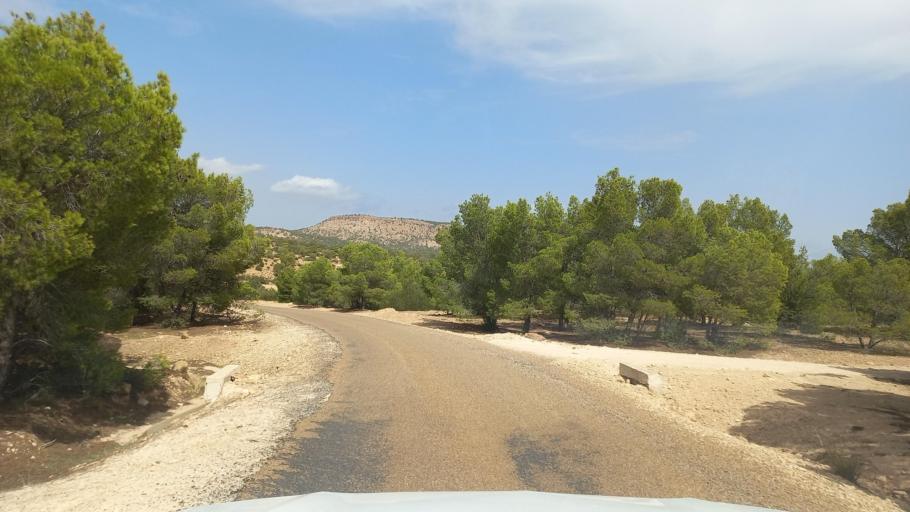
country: TN
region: Al Qasrayn
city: Sbiba
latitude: 35.4086
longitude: 8.9289
